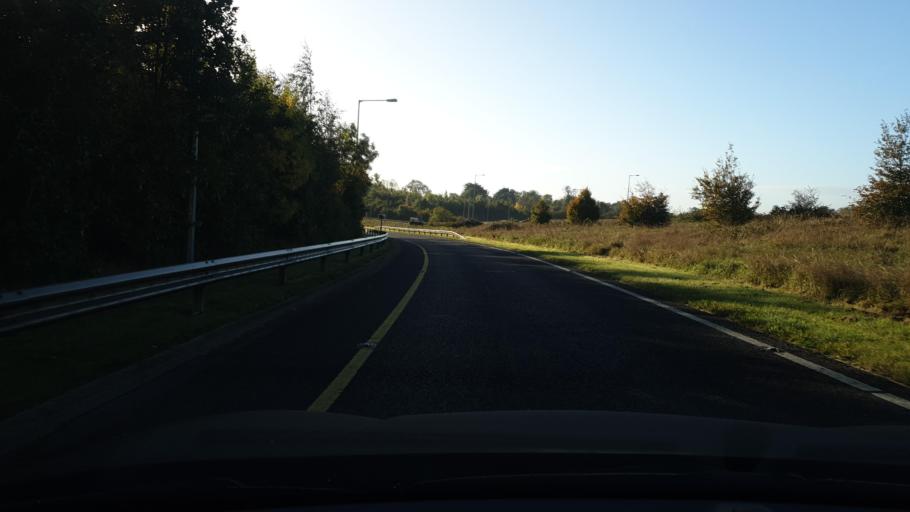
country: IE
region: Leinster
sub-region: An Mhi
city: Ashbourne
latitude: 53.4897
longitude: -6.3870
